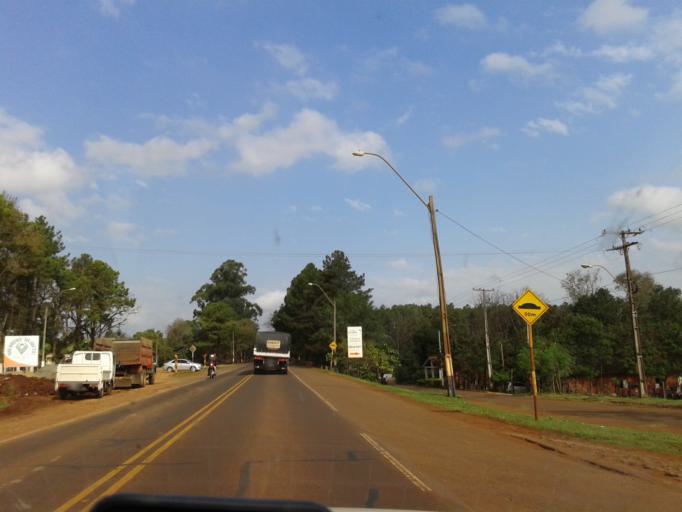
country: PY
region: Itapua
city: Arquitecto Tomas Romero Pereira
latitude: -26.4947
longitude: -55.2793
